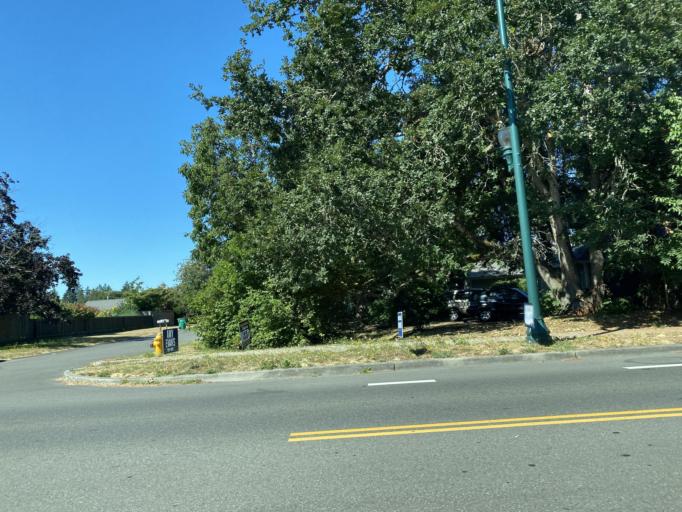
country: US
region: Washington
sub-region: Thurston County
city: Olympia
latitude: 47.0282
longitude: -122.8651
